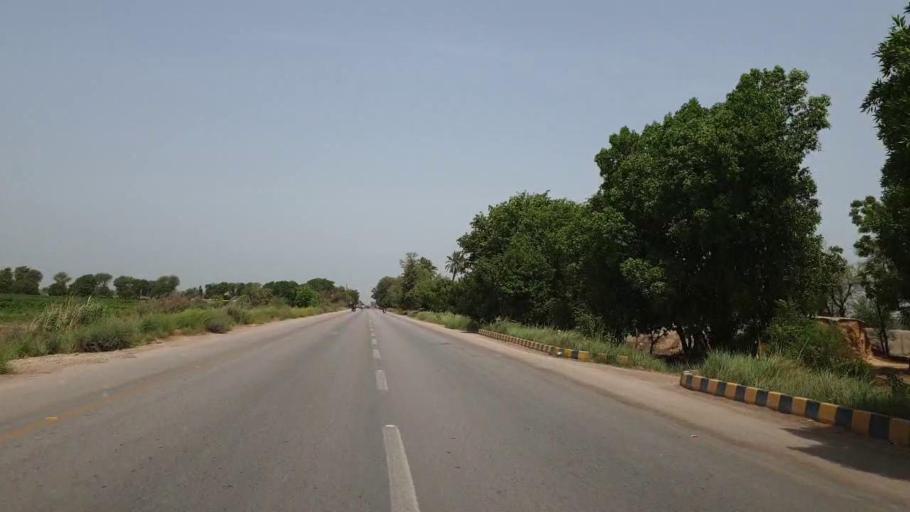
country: PK
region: Sindh
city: Nawabshah
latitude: 26.2196
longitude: 68.5014
